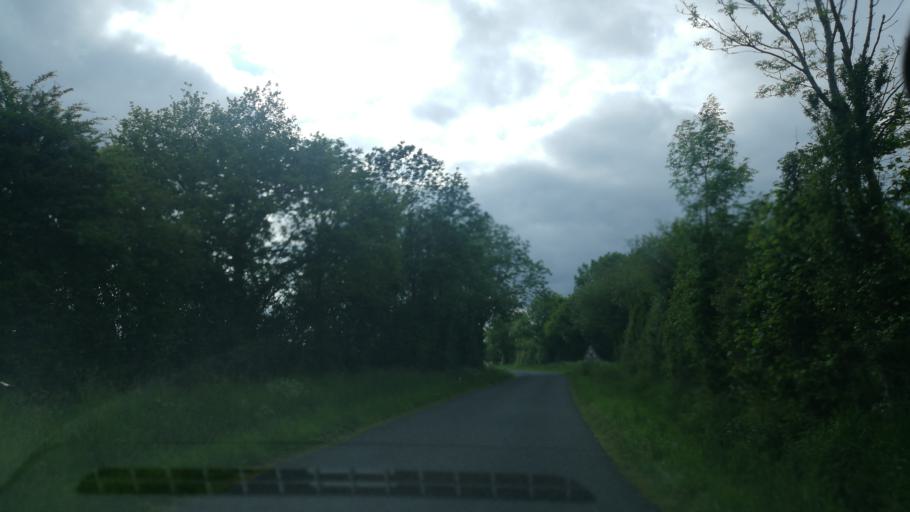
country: FR
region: Poitou-Charentes
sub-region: Departement des Deux-Sevres
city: Moncoutant
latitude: 46.7025
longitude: -0.5794
